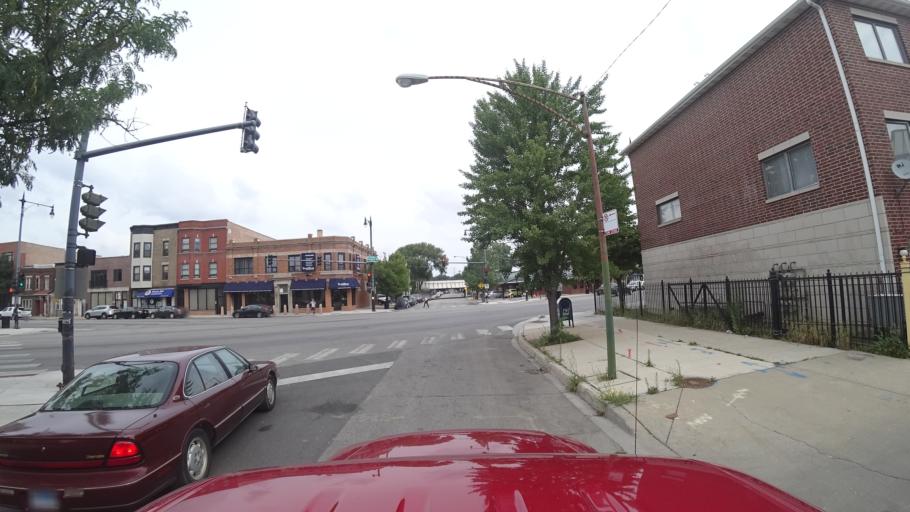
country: US
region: Illinois
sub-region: Cook County
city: Chicago
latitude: 41.8300
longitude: -87.6777
